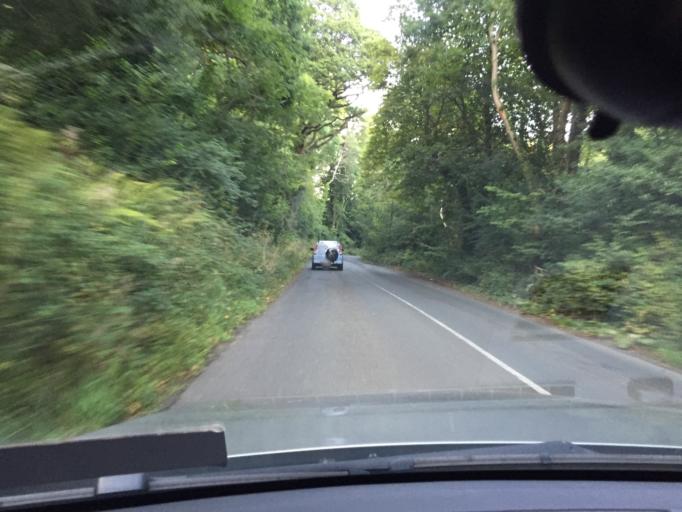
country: IE
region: Leinster
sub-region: Wicklow
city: Enniskerry
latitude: 53.1785
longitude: -6.1744
